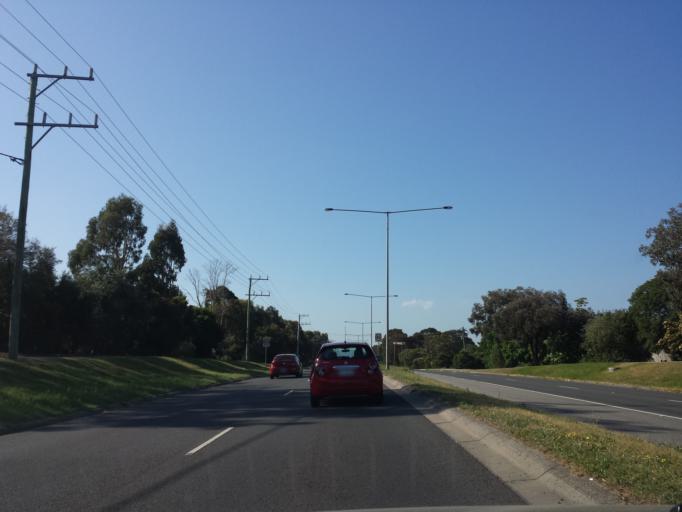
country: AU
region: Victoria
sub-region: Casey
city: Narre Warren North
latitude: -38.0072
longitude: 145.3106
